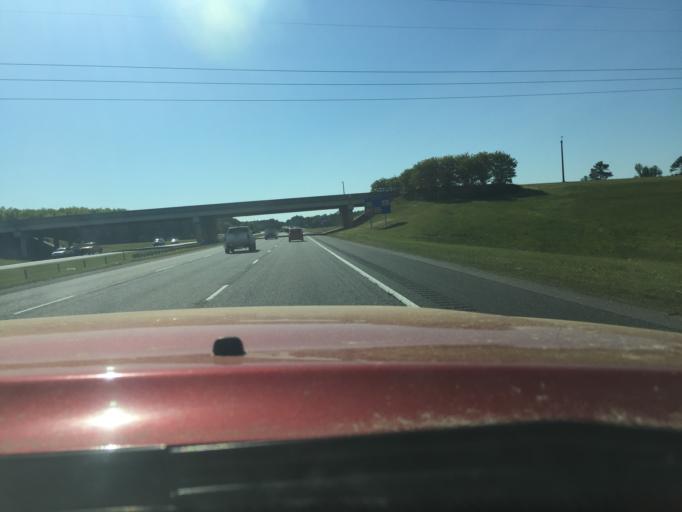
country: US
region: South Carolina
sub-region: Lexington County
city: Cayce
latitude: 33.9293
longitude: -81.0412
